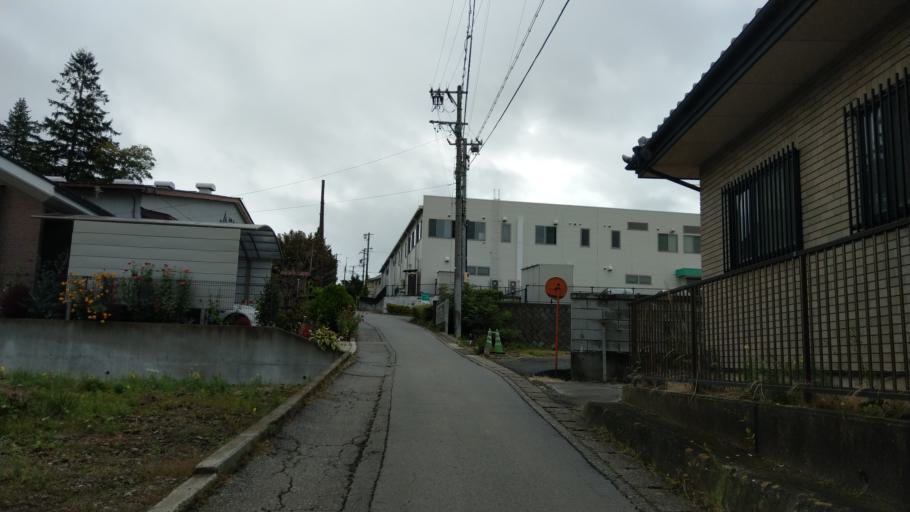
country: JP
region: Nagano
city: Komoro
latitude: 36.3181
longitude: 138.4356
